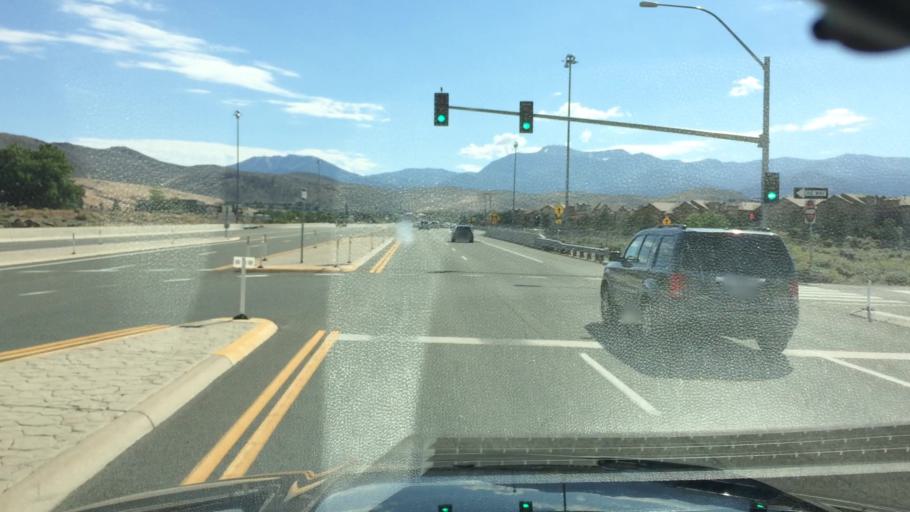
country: US
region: Nevada
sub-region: Washoe County
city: Sparks
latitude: 39.3963
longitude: -119.7596
